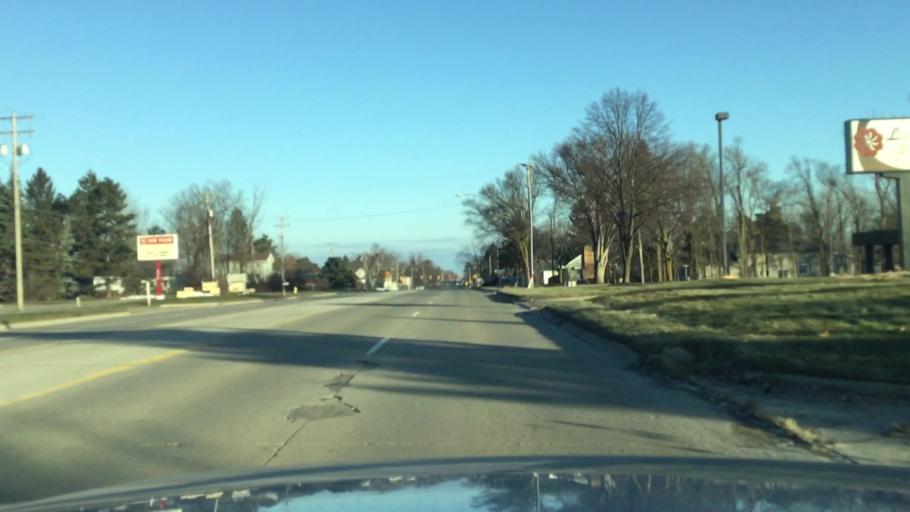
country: US
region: Michigan
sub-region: Genesee County
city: Flushing
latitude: 43.0569
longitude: -83.7728
